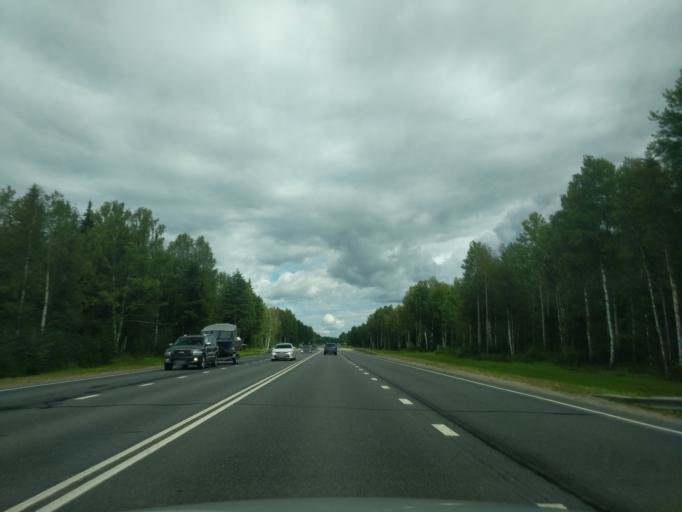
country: RU
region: Jaroslavl
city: Nekrasovskoye
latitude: 57.5889
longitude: 40.2972
